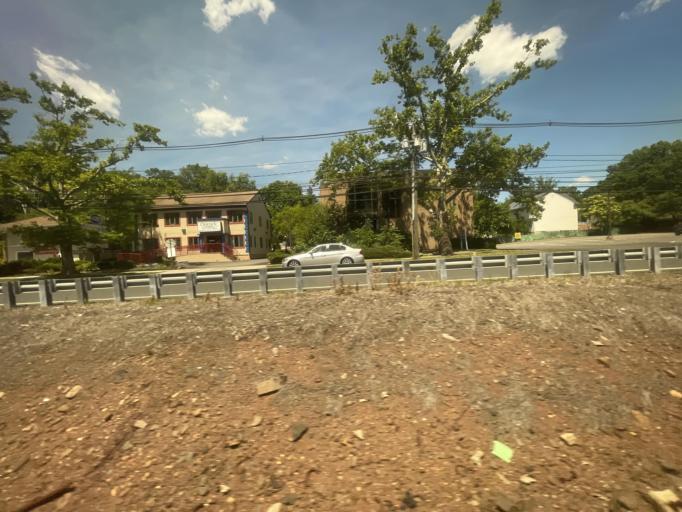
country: US
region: New Jersey
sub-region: Middlesex County
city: Iselin
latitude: 40.5632
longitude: -74.3350
